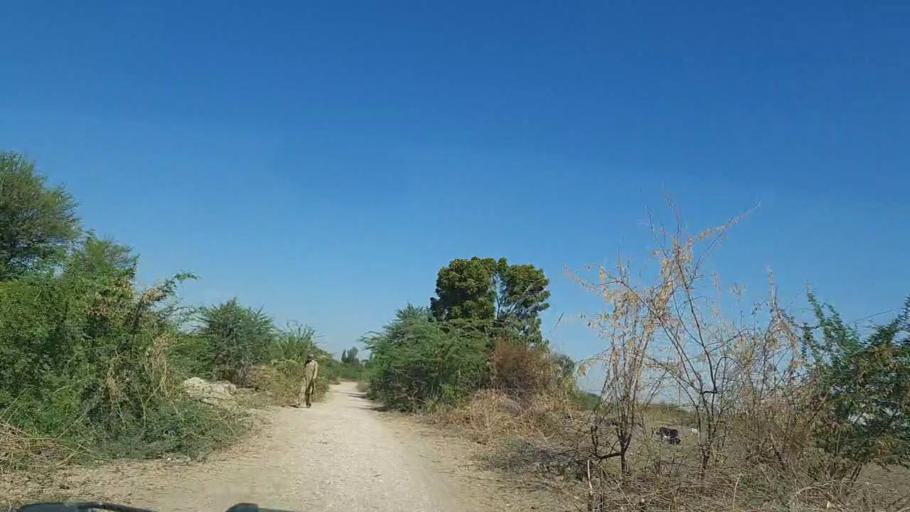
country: PK
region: Sindh
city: Dhoro Naro
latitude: 25.4736
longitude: 69.5128
